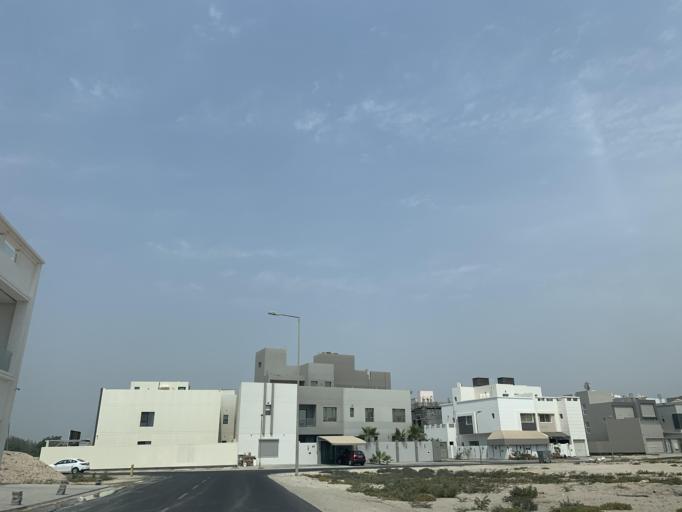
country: BH
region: Manama
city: Jidd Hafs
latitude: 26.2132
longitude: 50.4847
